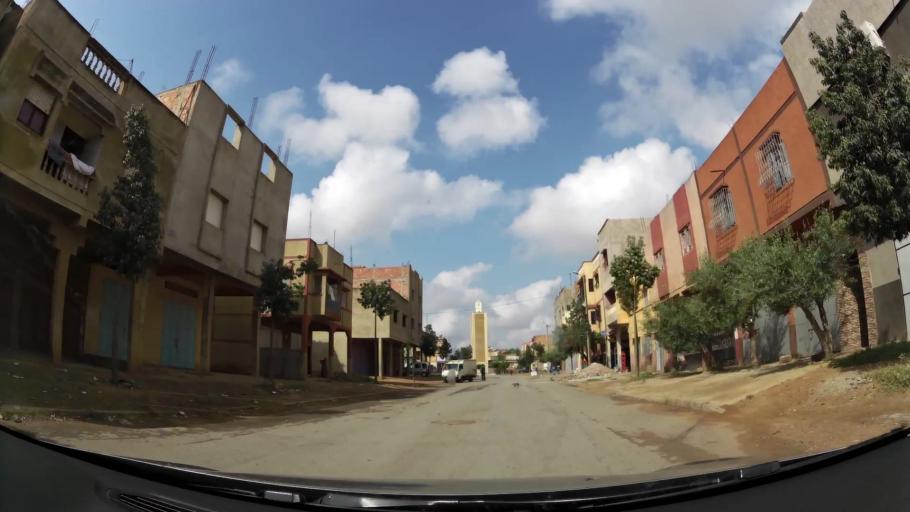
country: MA
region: Rabat-Sale-Zemmour-Zaer
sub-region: Khemisset
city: Tiflet
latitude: 33.8997
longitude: -6.3167
